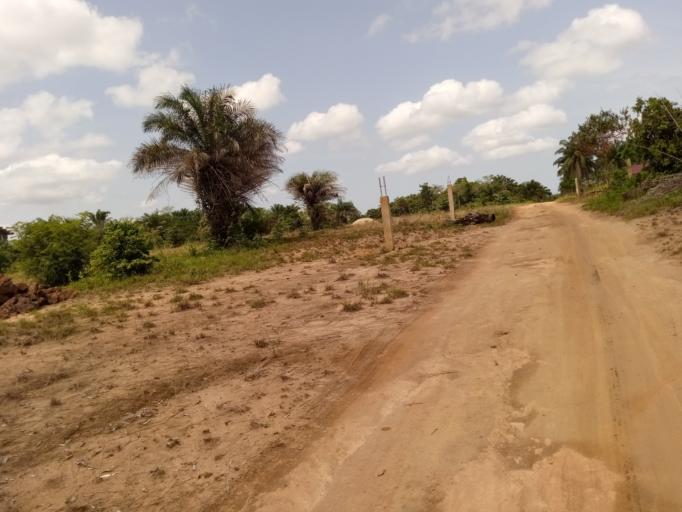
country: SL
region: Western Area
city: Waterloo
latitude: 8.3577
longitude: -13.0104
